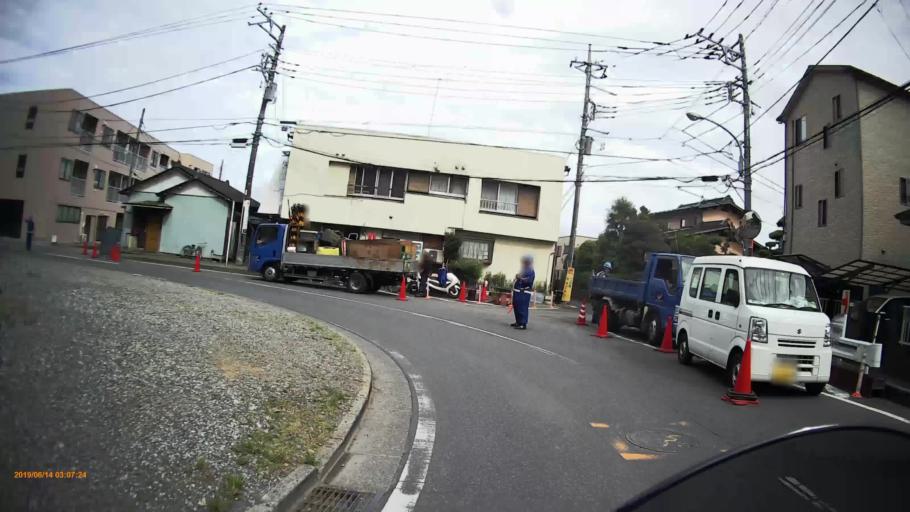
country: JP
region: Kanagawa
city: Minami-rinkan
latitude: 35.4123
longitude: 139.4539
